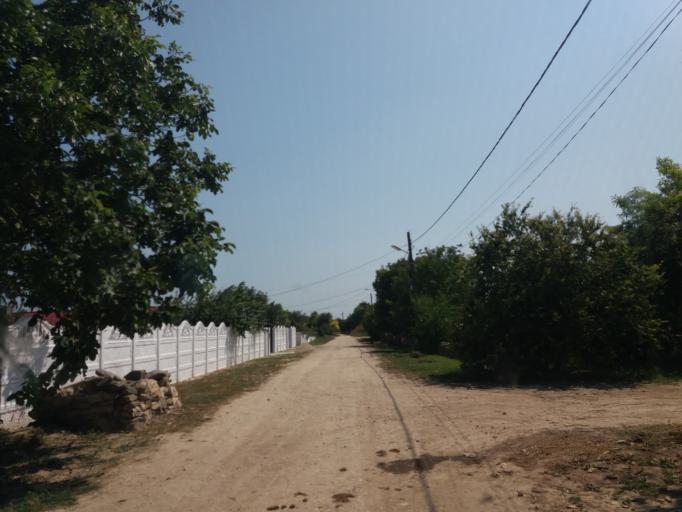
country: RO
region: Constanta
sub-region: Comuna Sacele
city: Sacele
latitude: 44.4550
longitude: 28.7379
